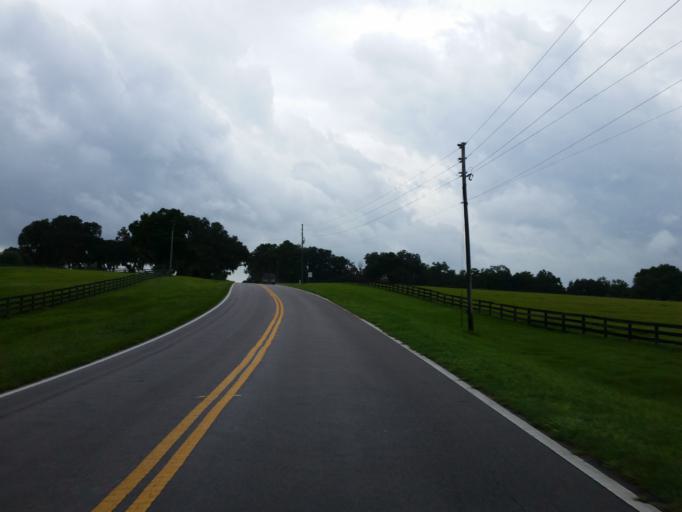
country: US
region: Florida
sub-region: Marion County
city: Citra
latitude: 29.4102
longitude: -82.2583
